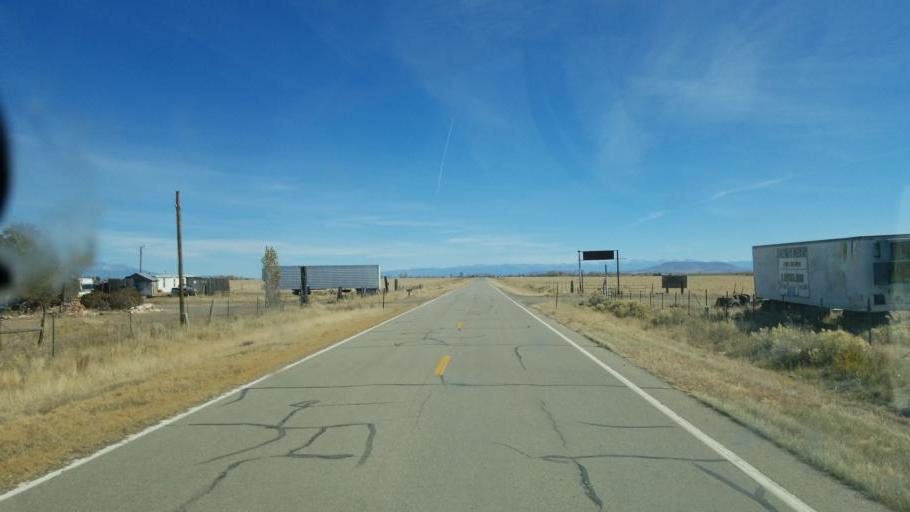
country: US
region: Colorado
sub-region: Conejos County
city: Conejos
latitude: 37.2833
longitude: -106.1439
